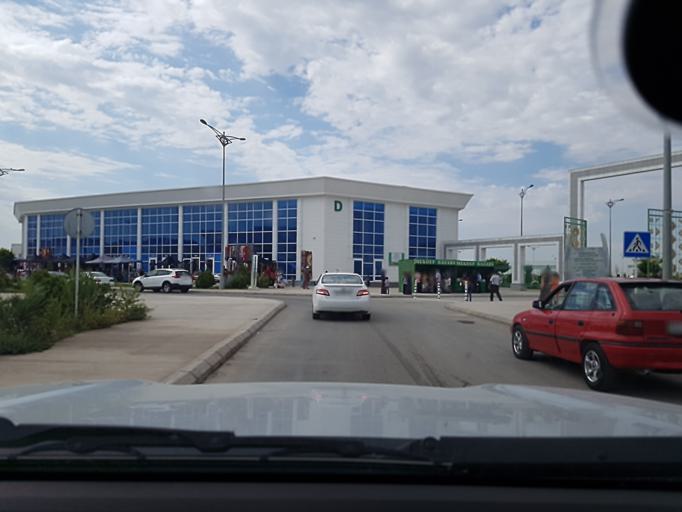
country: TM
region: Dasoguz
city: Dasoguz
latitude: 41.8773
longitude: 59.9496
